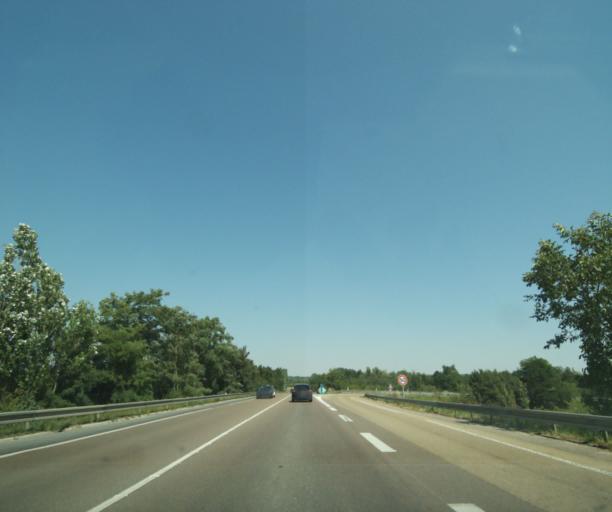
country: FR
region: Champagne-Ardenne
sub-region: Departement de la Marne
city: Frignicourt
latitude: 48.7231
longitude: 4.6280
